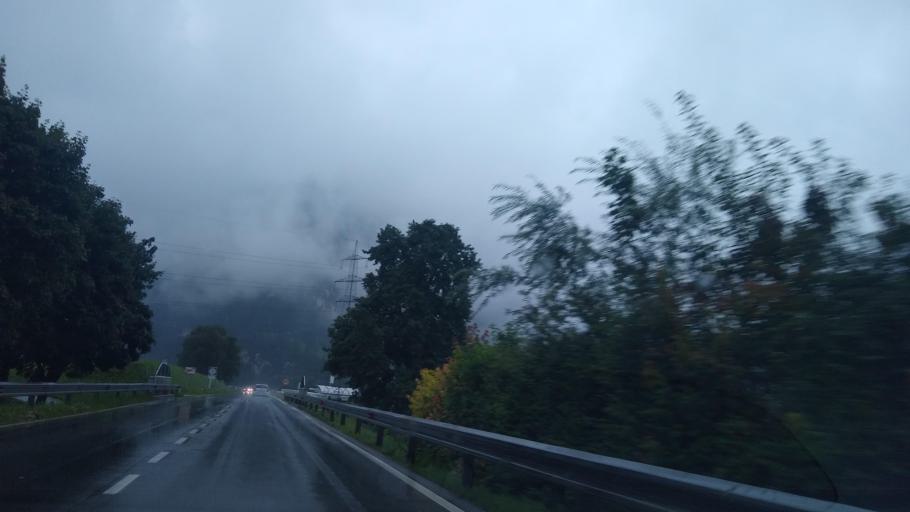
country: AT
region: Tyrol
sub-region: Politischer Bezirk Schwaz
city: Strass im Zillertal
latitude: 47.3982
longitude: 11.8269
